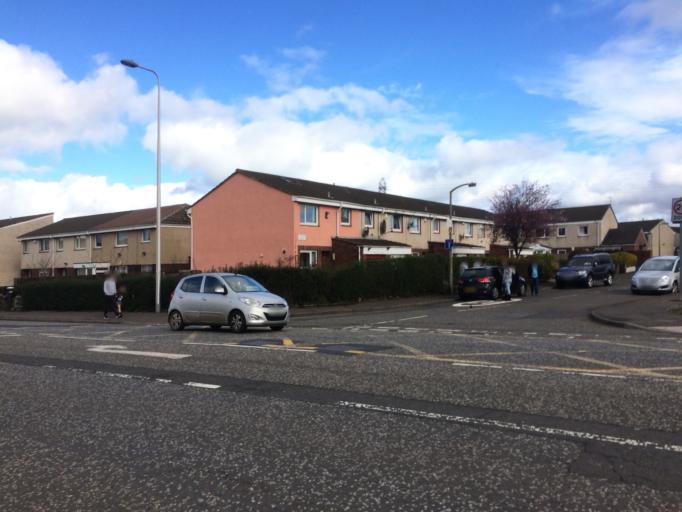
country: GB
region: Scotland
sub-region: West Lothian
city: Seafield
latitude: 55.9354
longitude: -3.1147
